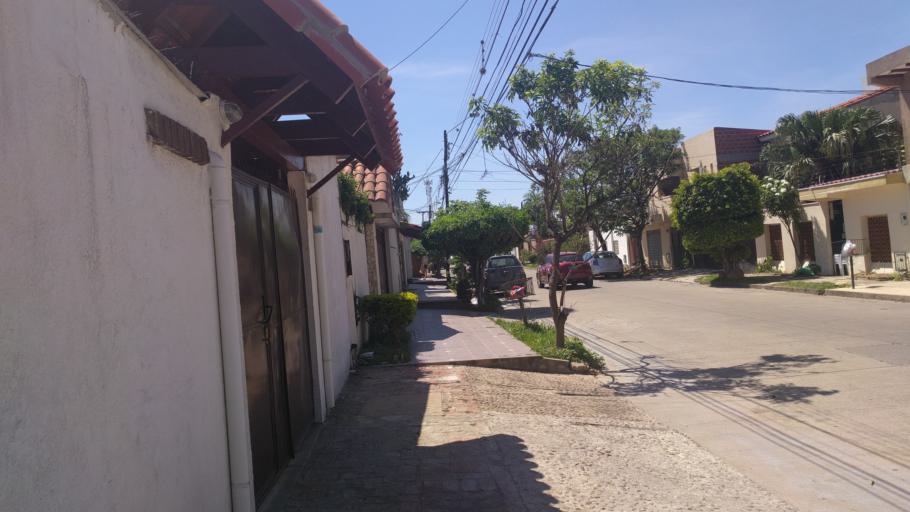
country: BO
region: Santa Cruz
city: Santa Cruz de la Sierra
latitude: -17.7554
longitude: -63.1638
